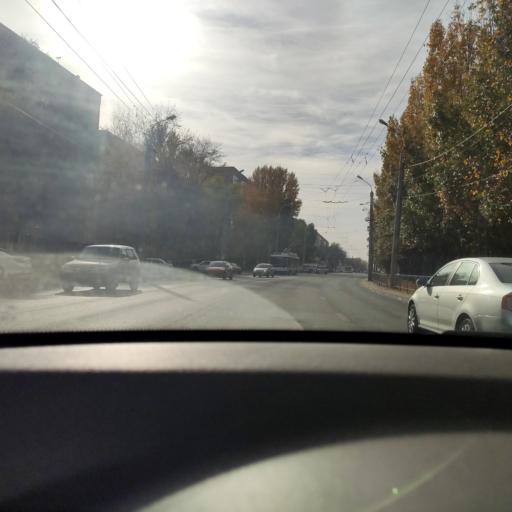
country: RU
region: Samara
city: Samara
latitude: 53.2377
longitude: 50.2262
